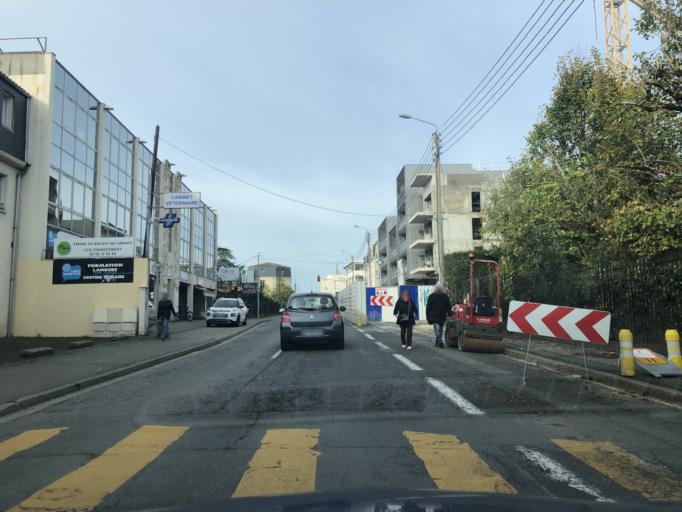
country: FR
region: Aquitaine
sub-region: Departement de la Gironde
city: Merignac
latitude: 44.8407
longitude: -0.6416
